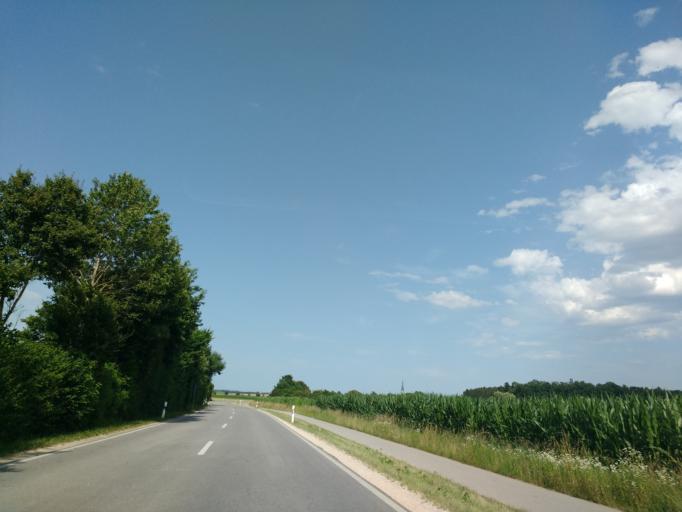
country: DE
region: Bavaria
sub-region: Upper Bavaria
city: Kienberg
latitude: 48.0326
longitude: 12.4446
